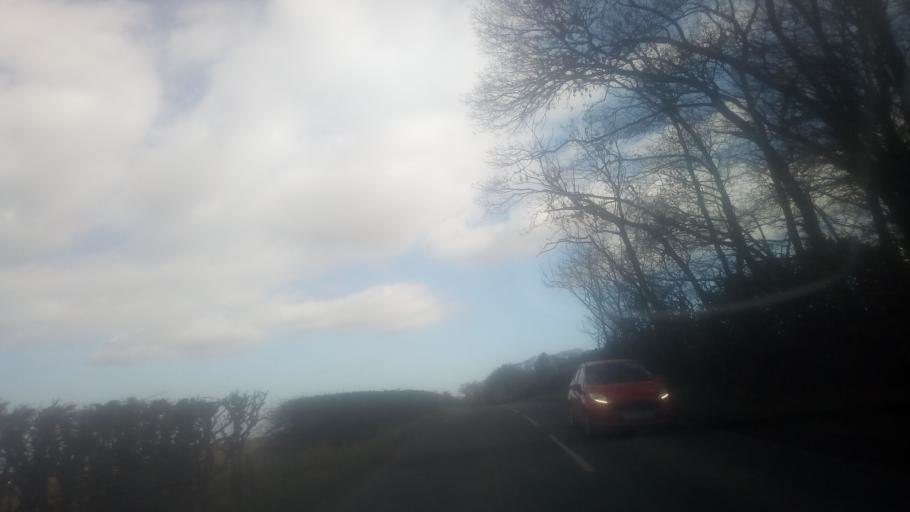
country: GB
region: Scotland
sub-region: East Lothian
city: Ormiston
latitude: 55.9019
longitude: -2.9455
